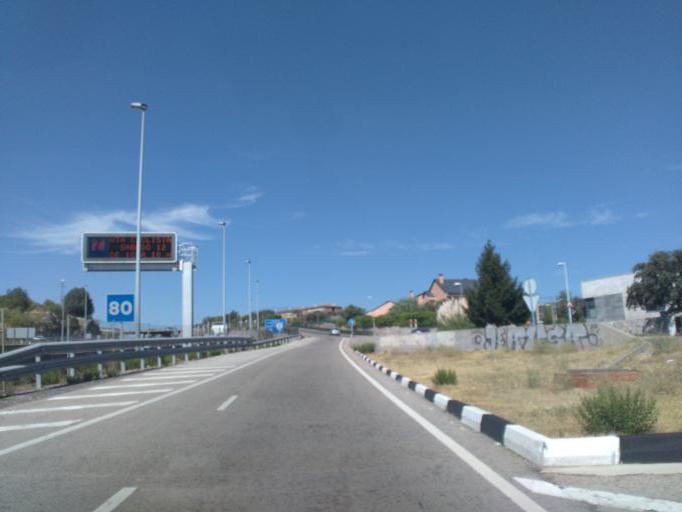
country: ES
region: Madrid
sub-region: Provincia de Madrid
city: Torrelodones
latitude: 40.5762
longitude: -3.9339
